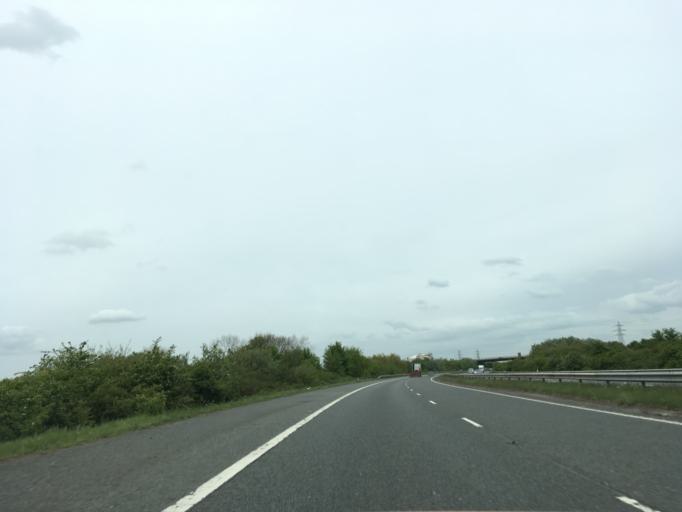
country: GB
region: England
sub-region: South Gloucestershire
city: Severn Beach
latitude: 51.5206
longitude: -2.6602
